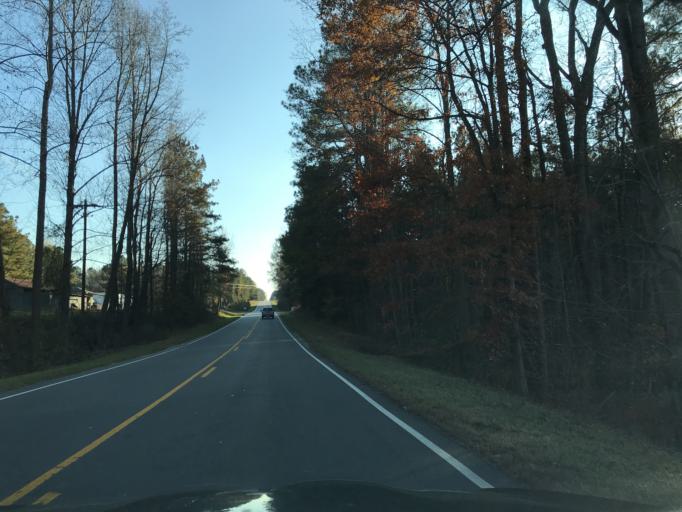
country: US
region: North Carolina
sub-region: Granville County
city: Creedmoor
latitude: 36.1058
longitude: -78.6886
